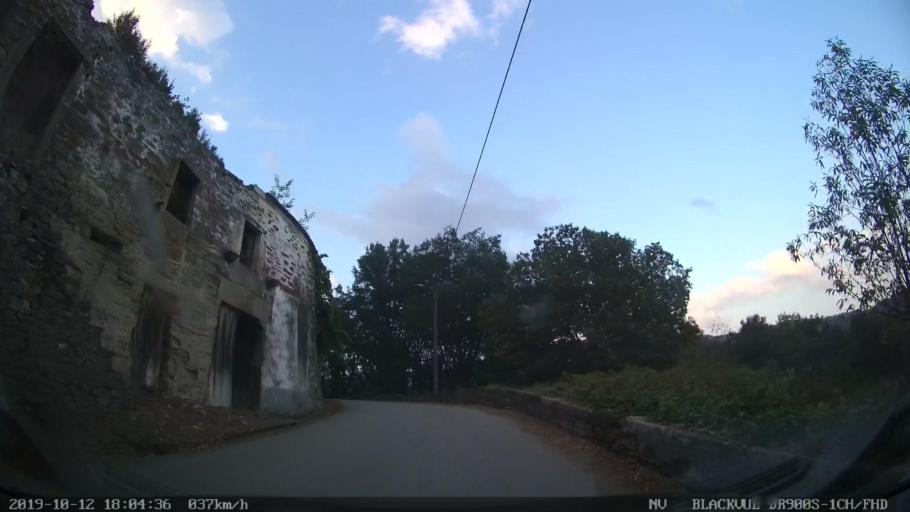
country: PT
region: Vila Real
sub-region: Mesao Frio
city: Mesao Frio
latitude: 41.1716
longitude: -7.8422
